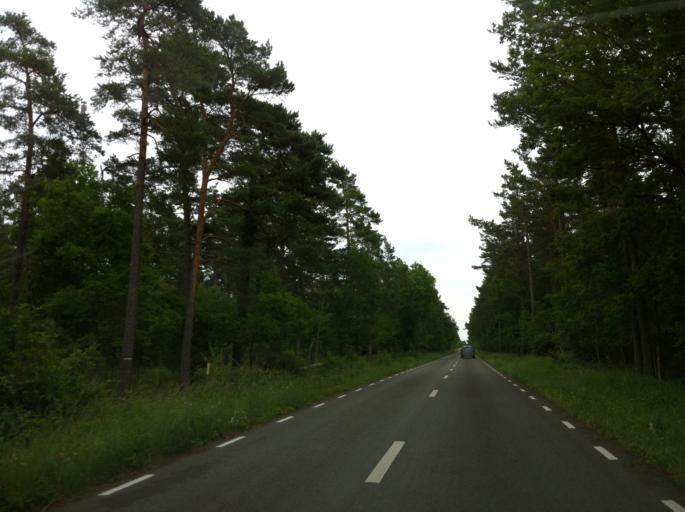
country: SE
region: Kalmar
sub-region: Vasterviks Kommun
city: Vaestervik
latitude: 57.3531
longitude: 17.0547
